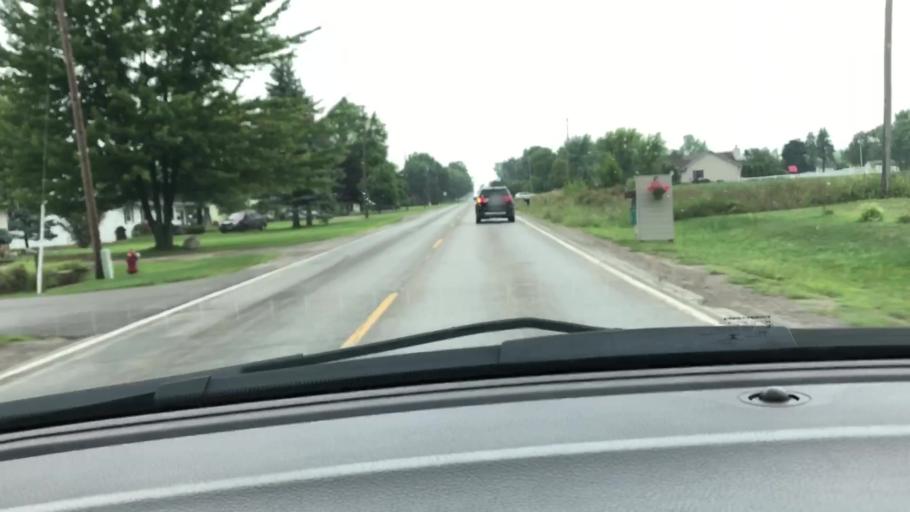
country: US
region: Michigan
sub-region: Saginaw County
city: Freeland
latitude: 43.4936
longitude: -84.0912
